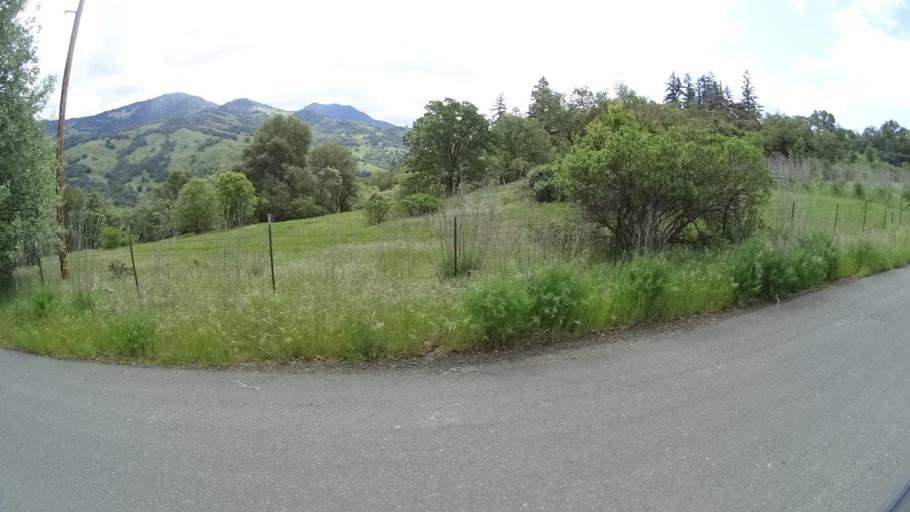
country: US
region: California
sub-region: Humboldt County
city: Redway
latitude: 40.1686
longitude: -123.6108
